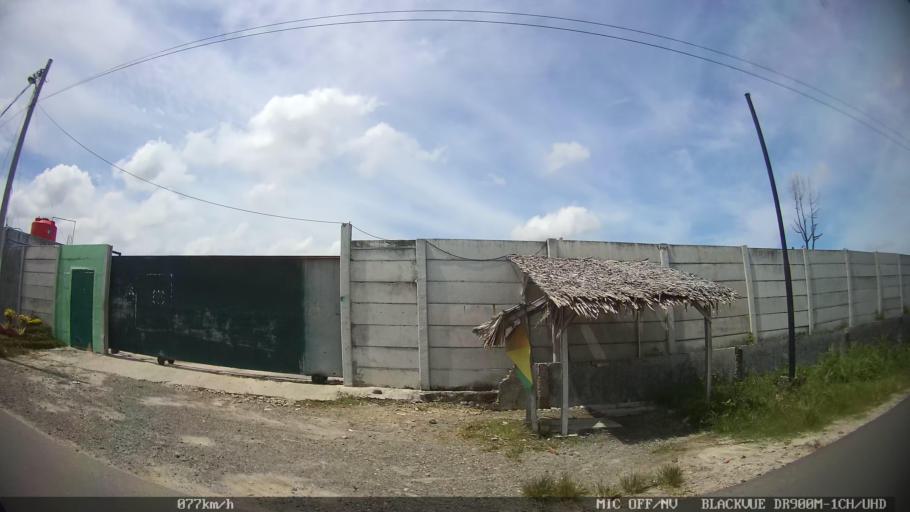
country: ID
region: North Sumatra
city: Percut
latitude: 3.5892
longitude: 98.8758
